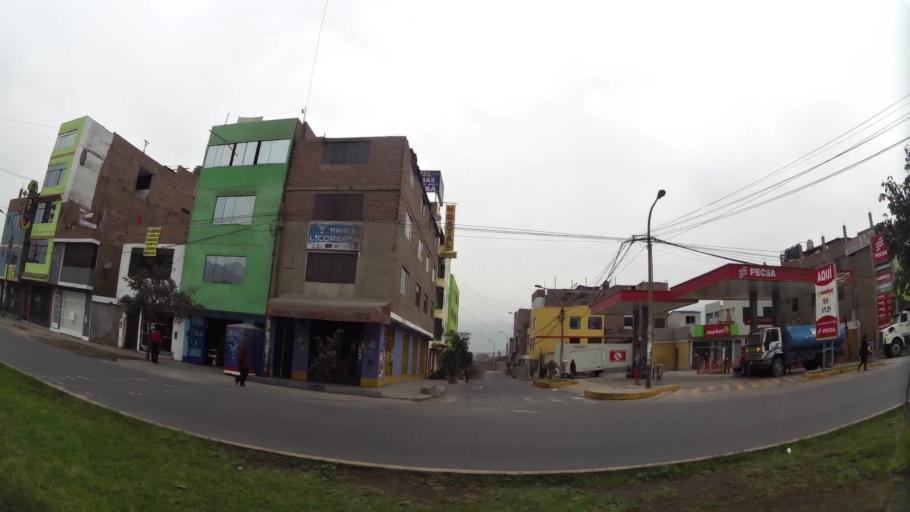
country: PE
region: Lima
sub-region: Lima
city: Independencia
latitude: -11.9715
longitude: -76.9922
